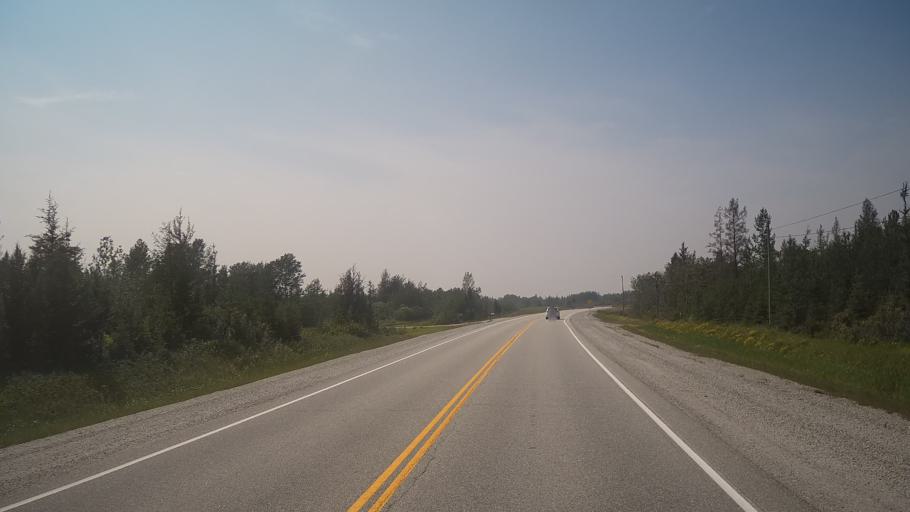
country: CA
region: Ontario
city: Kapuskasing
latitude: 49.2866
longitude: -81.7720
